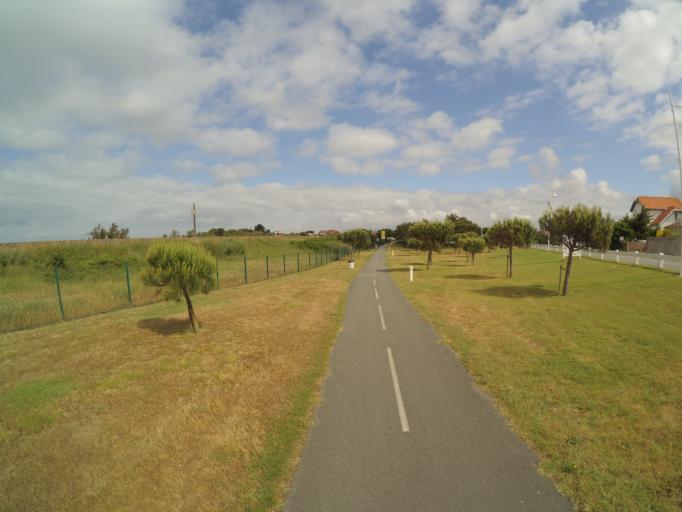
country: FR
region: Poitou-Charentes
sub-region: Departement de la Charente-Maritime
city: Angoulins
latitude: 46.0935
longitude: -1.0997
